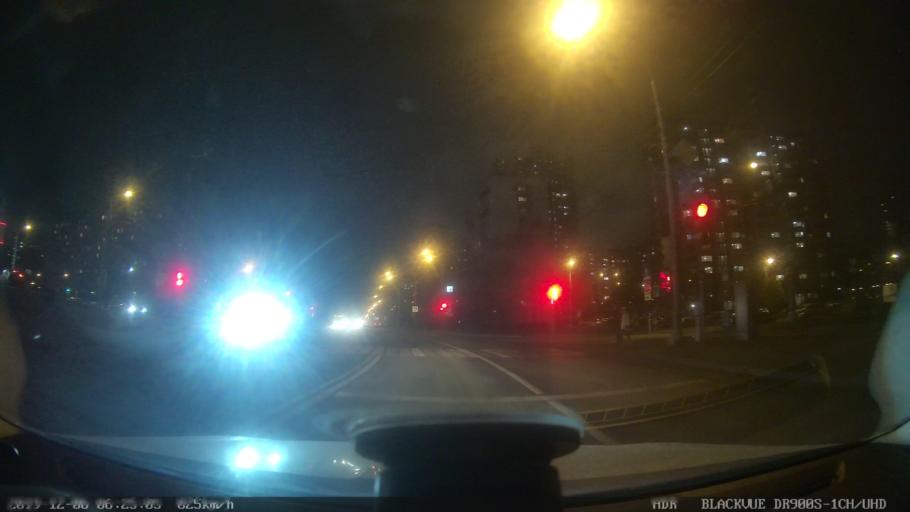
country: RU
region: Moscow
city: Leonovo
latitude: 55.8780
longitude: 37.6448
